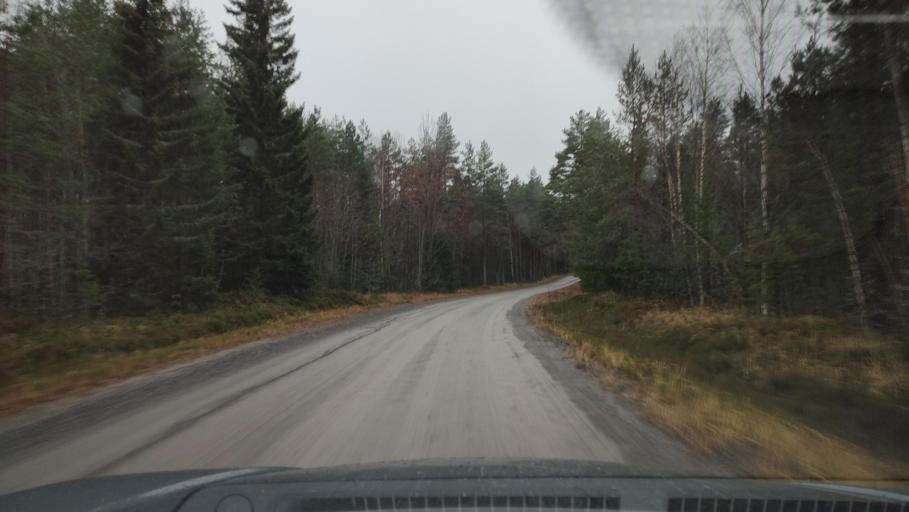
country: FI
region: Southern Ostrobothnia
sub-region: Suupohja
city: Karijoki
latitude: 62.1351
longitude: 21.6377
